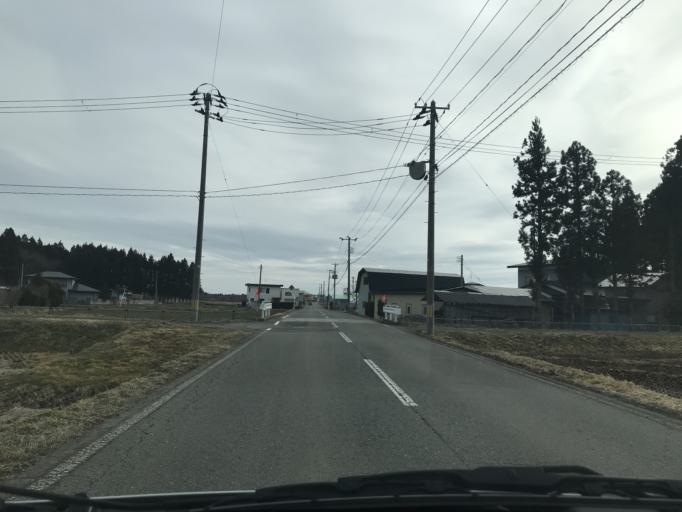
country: JP
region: Iwate
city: Hanamaki
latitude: 39.3906
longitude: 141.0743
